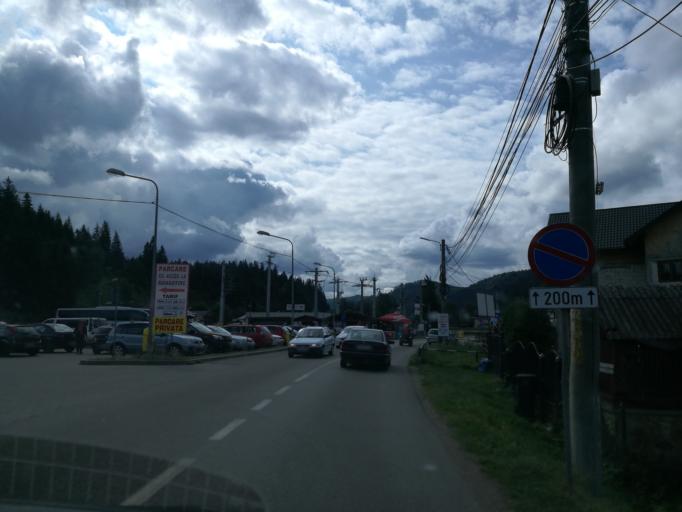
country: RO
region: Suceava
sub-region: Oras Gura Humorului
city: Gura Humorului
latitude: 47.5209
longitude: 25.8654
